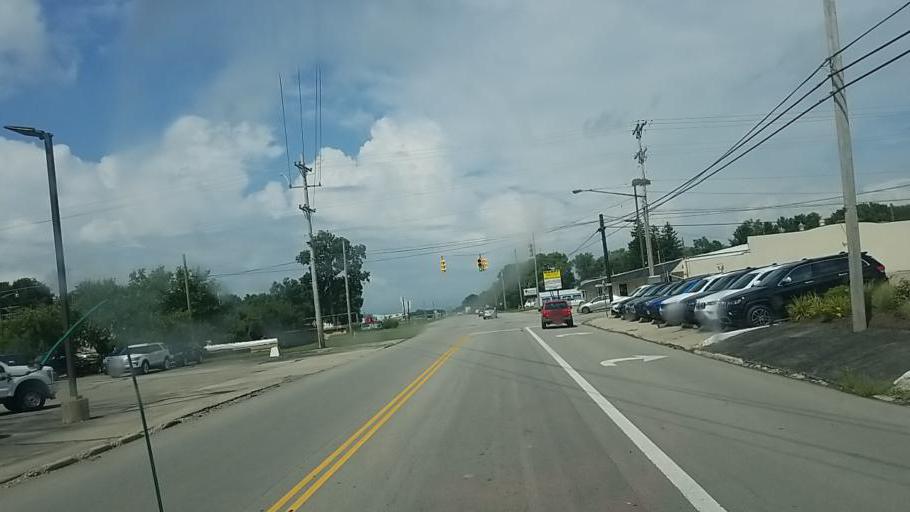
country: US
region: Ohio
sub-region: Champaign County
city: Urbana
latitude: 40.1256
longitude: -83.7490
